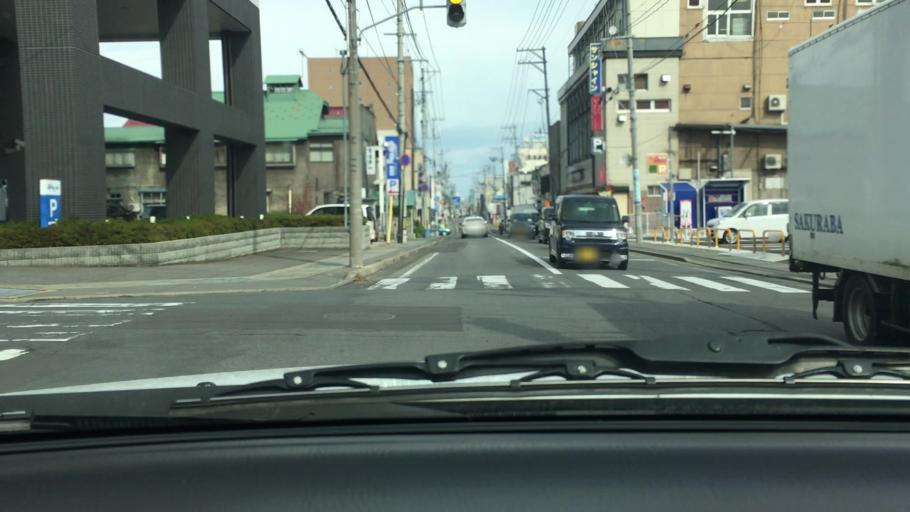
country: JP
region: Aomori
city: Hirosaki
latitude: 40.6004
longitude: 140.4688
